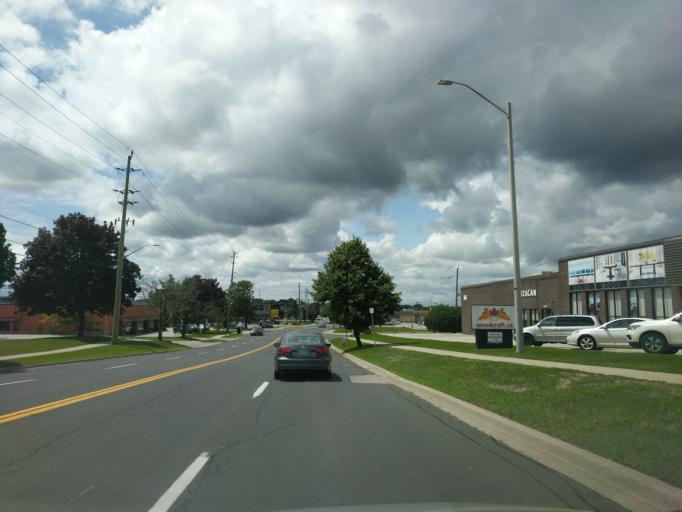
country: CA
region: Ontario
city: Willowdale
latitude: 43.8228
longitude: -79.3473
